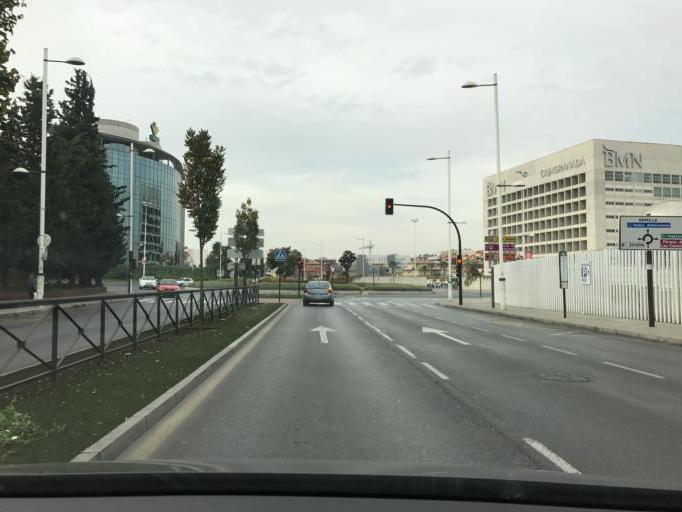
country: ES
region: Andalusia
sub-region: Provincia de Granada
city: Armilla
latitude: 37.1615
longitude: -3.6040
